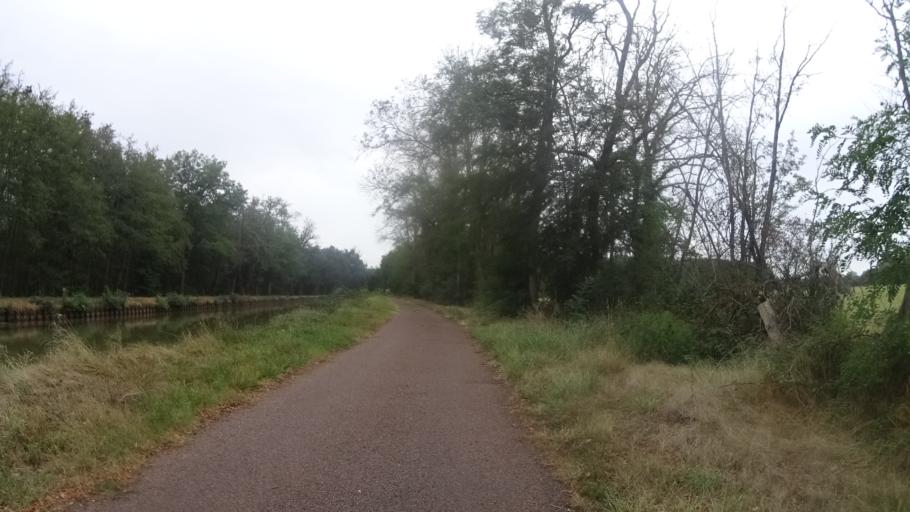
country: FR
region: Bourgogne
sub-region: Departement de la Nievre
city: Saint-Leger-des-Vignes
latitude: 46.8196
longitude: 3.4043
